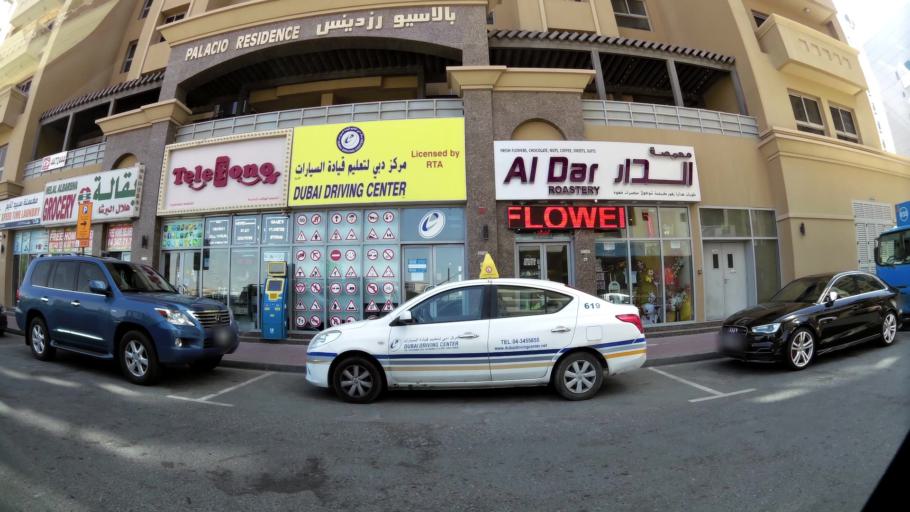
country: AE
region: Dubai
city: Dubai
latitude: 25.1127
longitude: 55.2064
